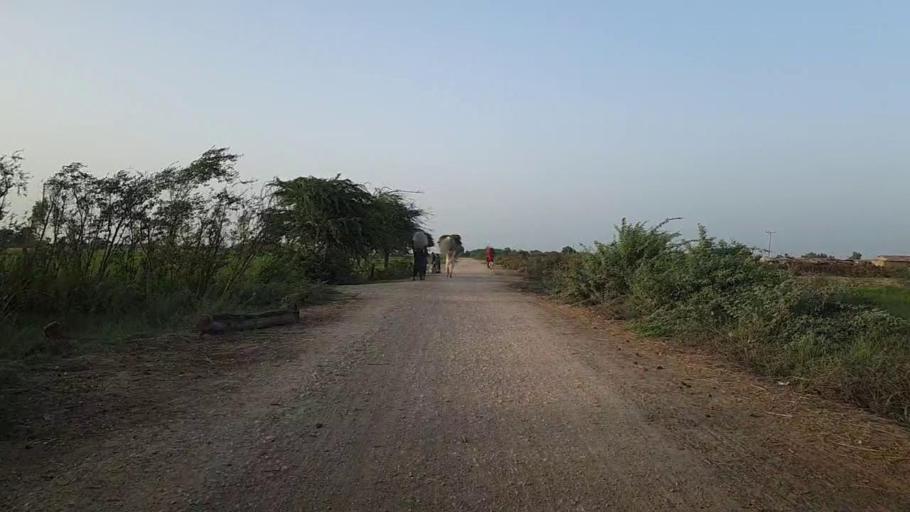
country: PK
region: Sindh
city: Kario
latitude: 24.7154
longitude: 68.4621
